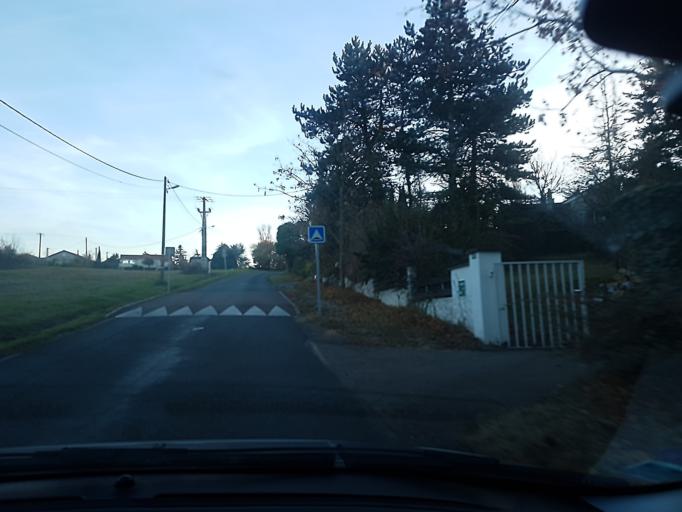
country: FR
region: Rhone-Alpes
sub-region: Departement du Rhone
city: Vourles
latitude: 45.6480
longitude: 4.7673
